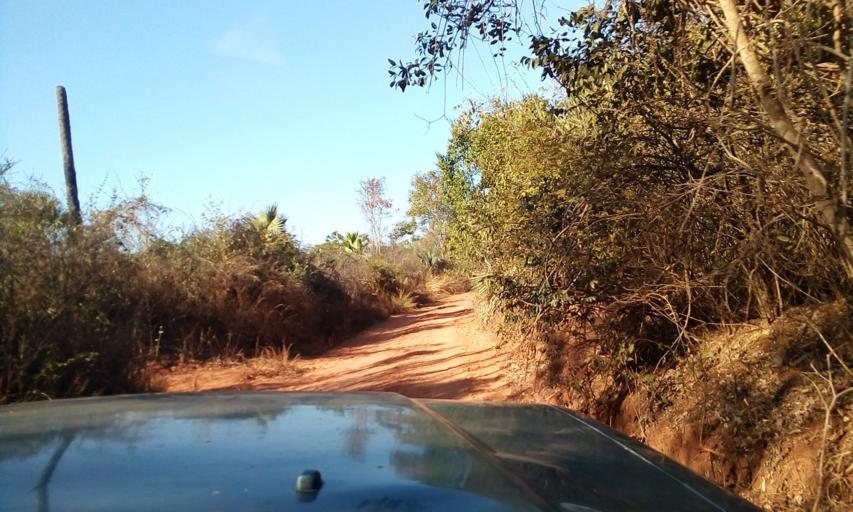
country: MG
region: Boeny
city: Sitampiky
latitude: -16.1915
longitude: 45.3621
